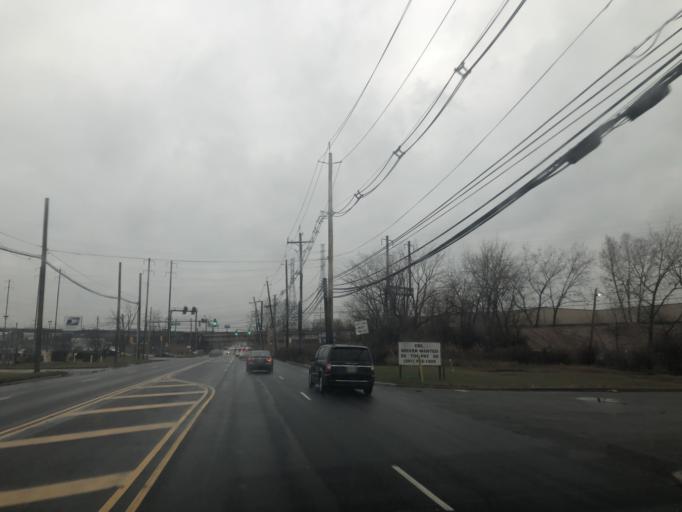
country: US
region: New Jersey
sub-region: Hudson County
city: Jersey City
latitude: 40.7475
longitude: -74.1087
